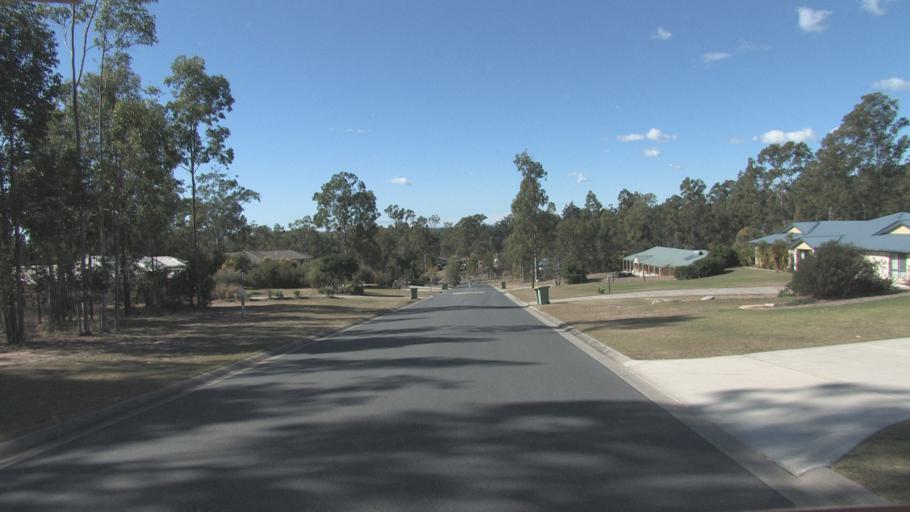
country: AU
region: Queensland
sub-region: Logan
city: North Maclean
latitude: -27.7543
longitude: 152.9377
